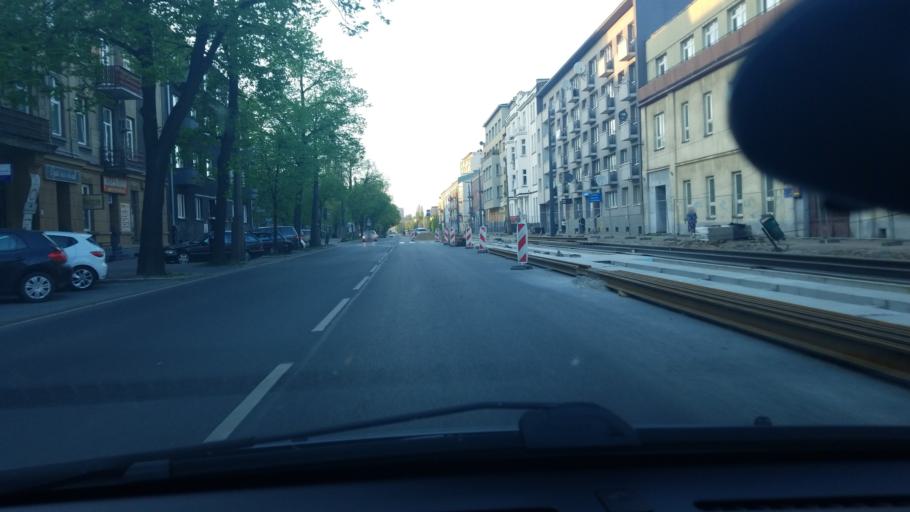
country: PL
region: Silesian Voivodeship
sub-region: Czestochowa
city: Czestochowa
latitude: 50.8133
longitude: 19.1183
